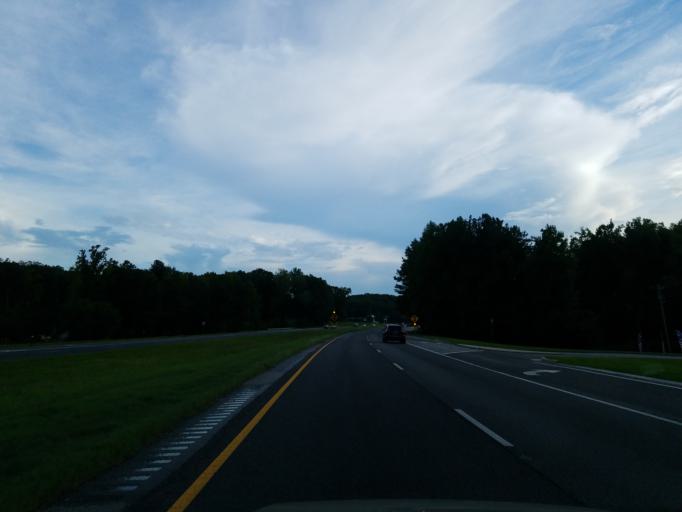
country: US
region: Georgia
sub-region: Forsyth County
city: Cumming
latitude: 34.2752
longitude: -84.0774
